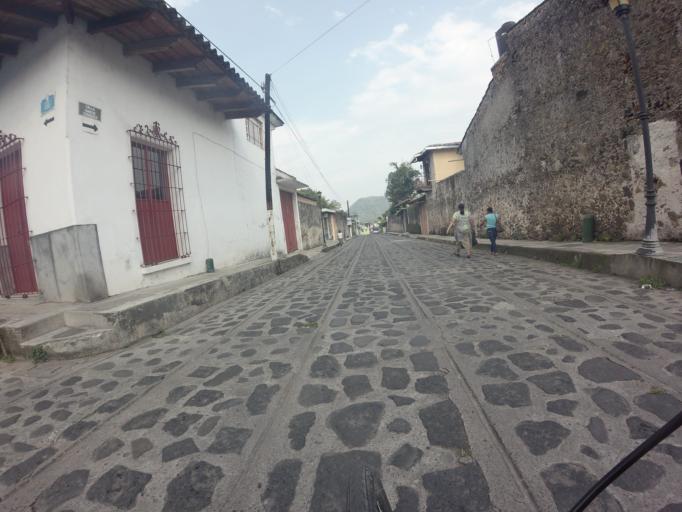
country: MX
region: Veracruz
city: Xico
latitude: 19.4199
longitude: -97.0049
